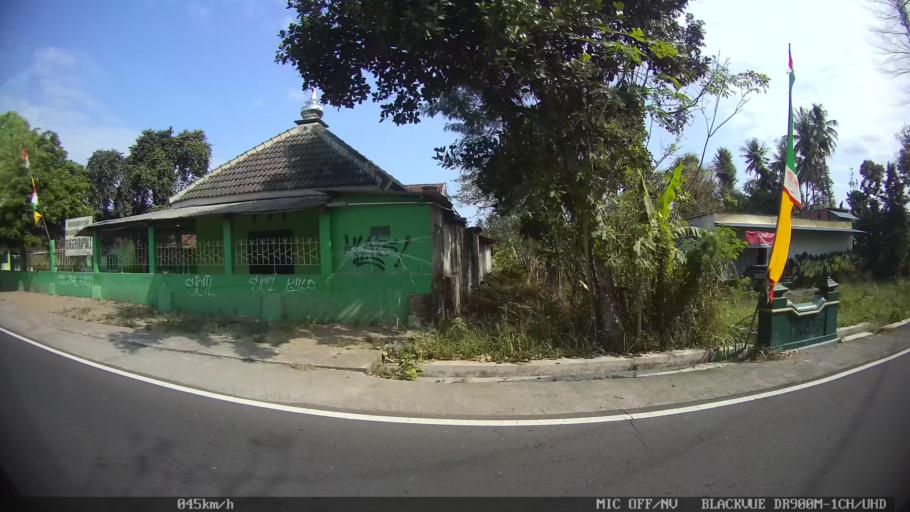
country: ID
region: Daerah Istimewa Yogyakarta
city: Depok
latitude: -7.7277
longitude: 110.4251
